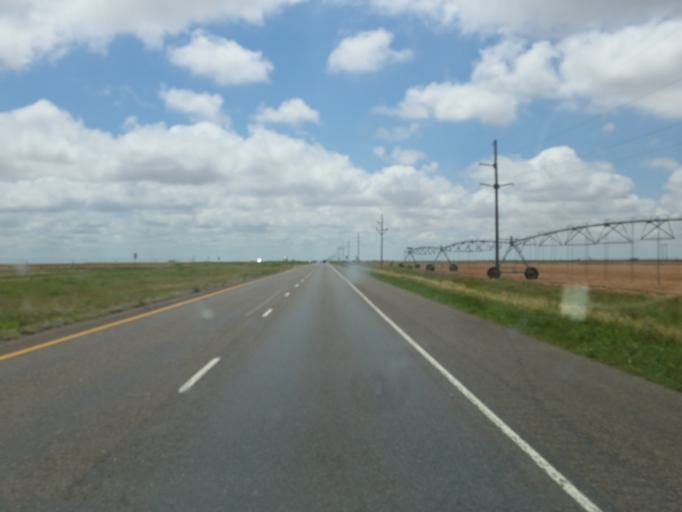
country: US
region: Texas
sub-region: Lubbock County
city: Slaton
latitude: 33.3934
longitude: -101.6036
